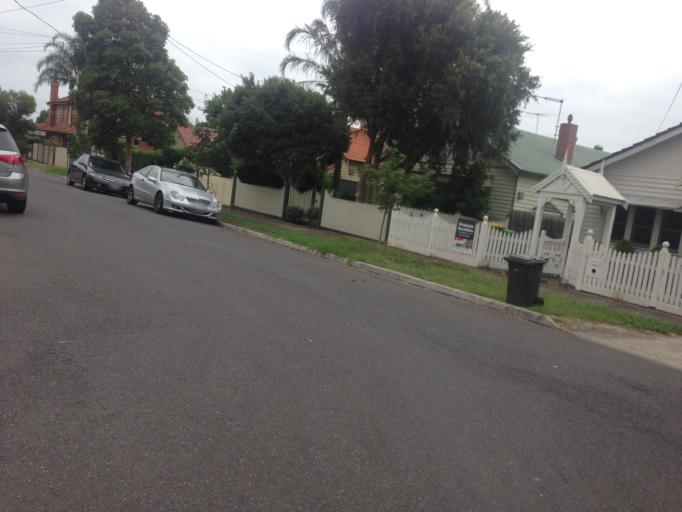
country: AU
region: Victoria
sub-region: Darebin
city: Thornbury
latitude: -37.7628
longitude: 145.0034
